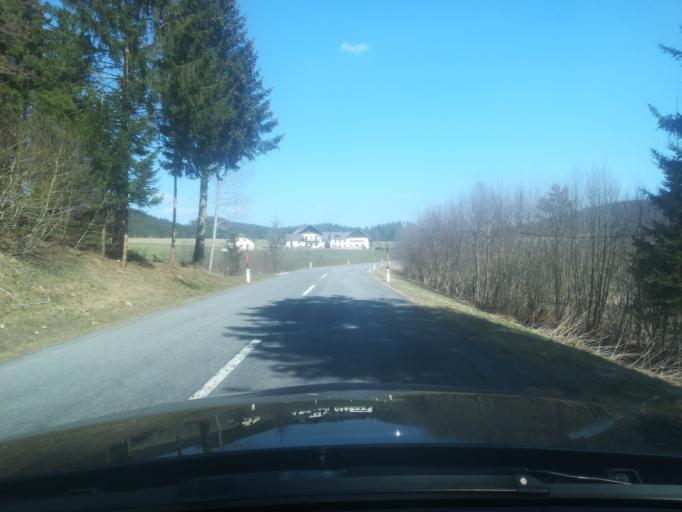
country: AT
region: Lower Austria
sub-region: Politischer Bezirk Zwettl
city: Langschlag
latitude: 48.4876
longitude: 14.8079
